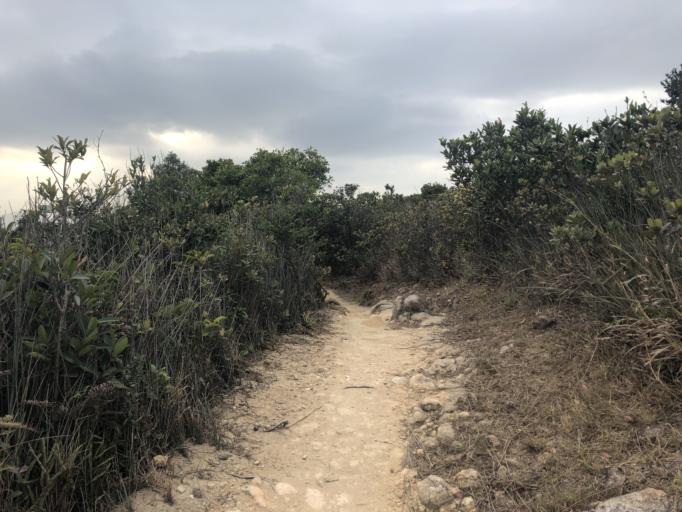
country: HK
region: Wanchai
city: Wan Chai
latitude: 22.2688
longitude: 114.2090
